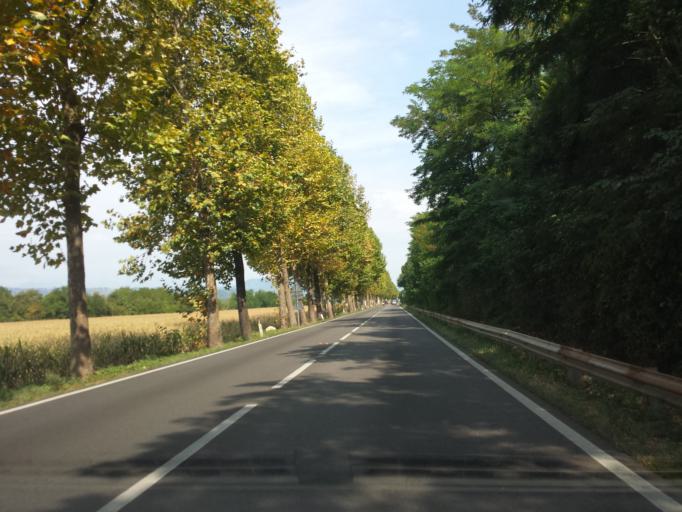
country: IT
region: Veneto
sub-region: Provincia di Vicenza
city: Tezze
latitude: 45.5273
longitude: 11.3863
